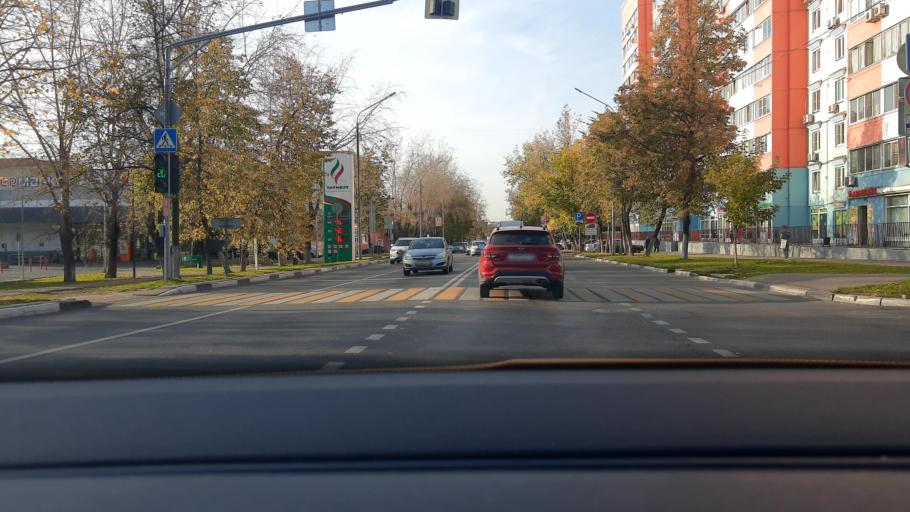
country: RU
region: Moskovskaya
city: Reutov
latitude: 55.7663
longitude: 37.8497
